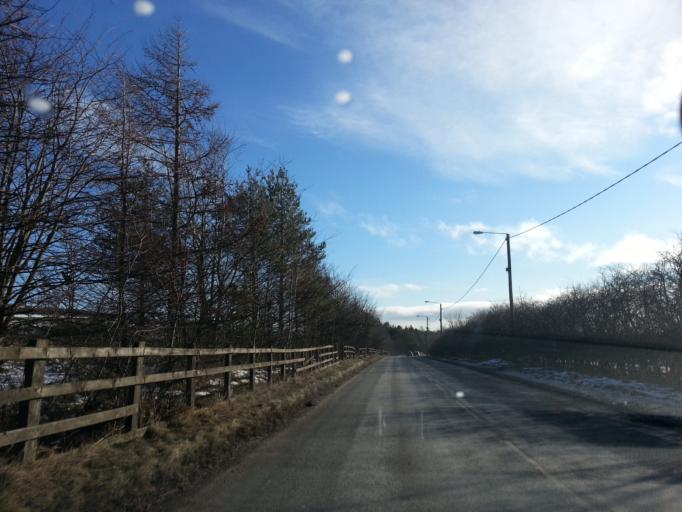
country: GB
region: England
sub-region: County Durham
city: Crook
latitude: 54.7271
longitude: -1.7509
